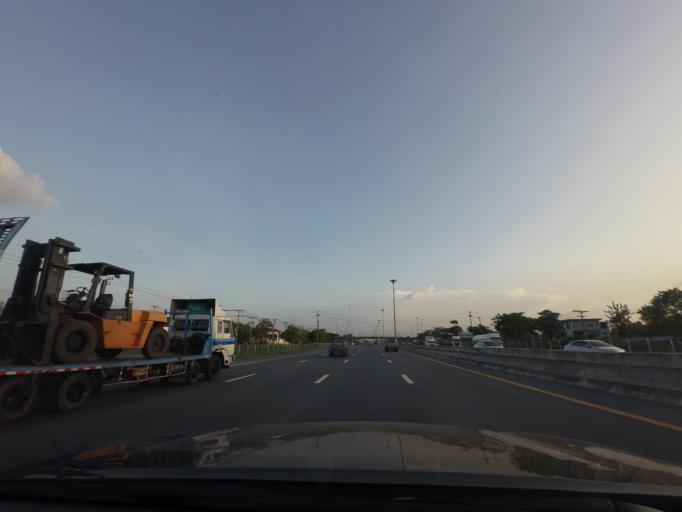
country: TH
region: Pathum Thani
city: Khlong Luang
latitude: 14.0707
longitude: 100.6964
